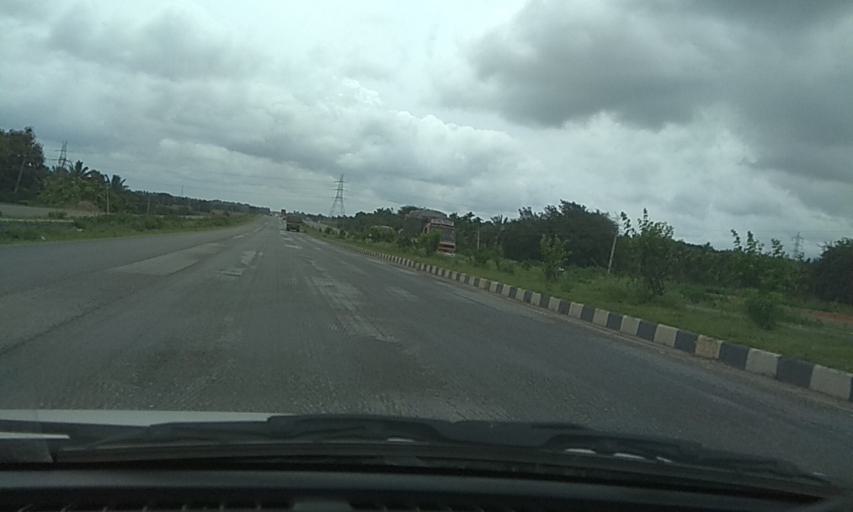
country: IN
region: Karnataka
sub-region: Davanagere
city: Mayakonda
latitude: 14.3702
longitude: 76.1312
